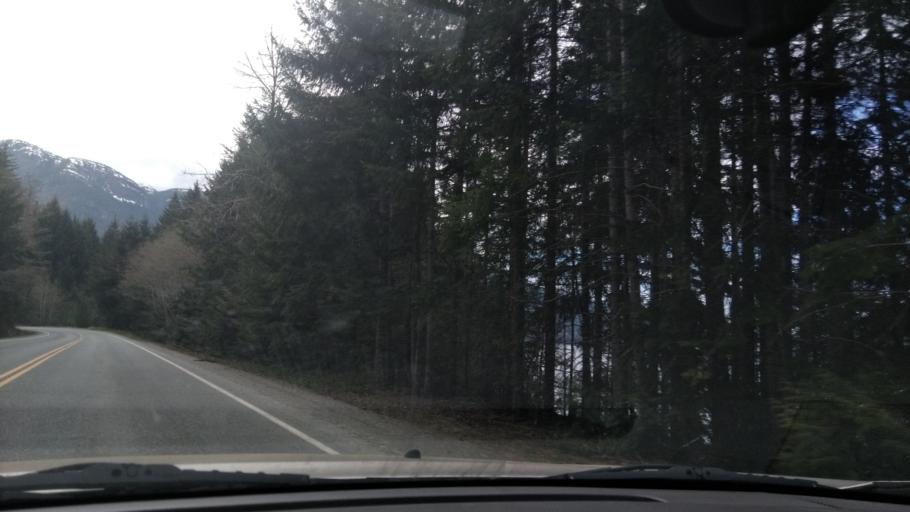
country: CA
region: British Columbia
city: Campbell River
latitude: 49.8770
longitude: -125.6707
